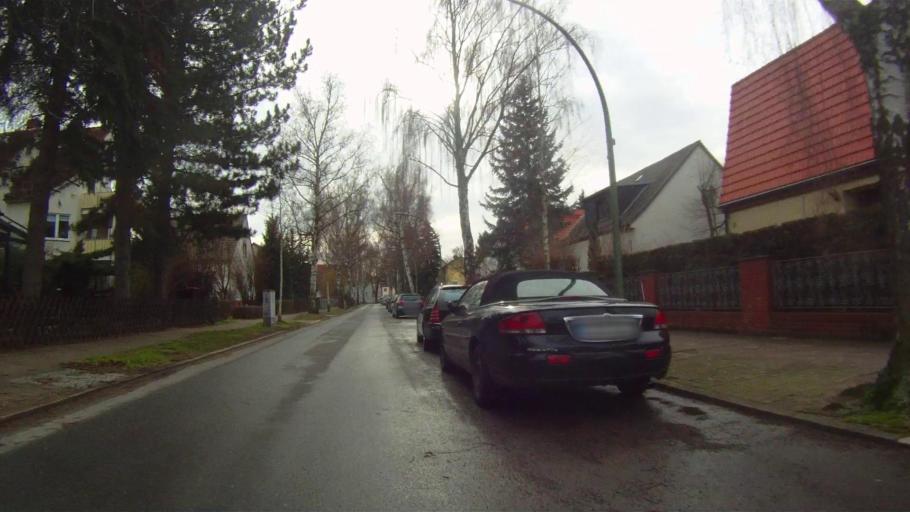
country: DE
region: Berlin
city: Lichtenrade
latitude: 52.3872
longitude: 13.4250
